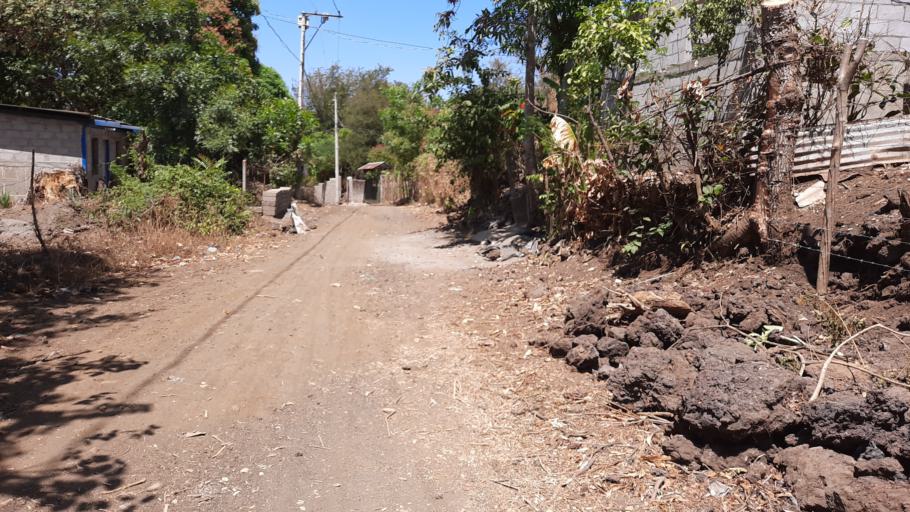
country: NI
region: Masaya
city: Ticuantepe
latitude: 12.0305
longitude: -86.1667
